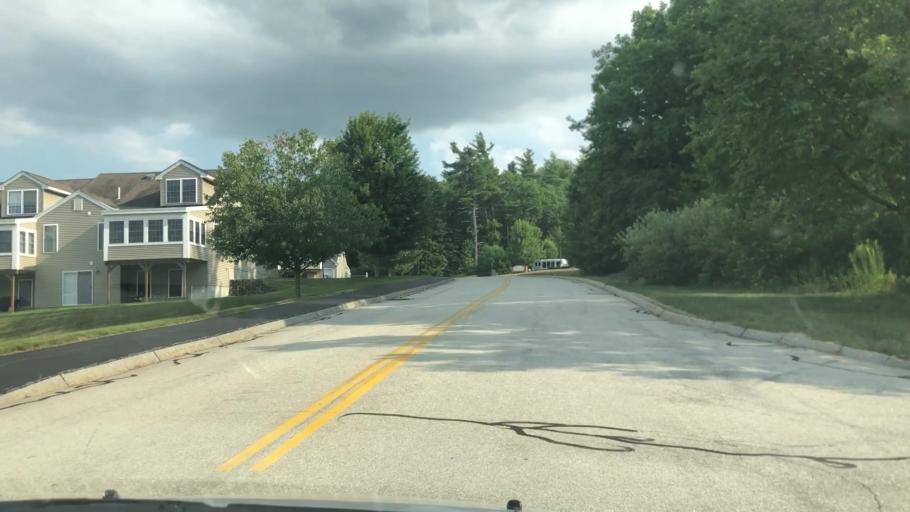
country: US
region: New Hampshire
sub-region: Hillsborough County
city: Milford
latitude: 42.8270
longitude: -71.6429
